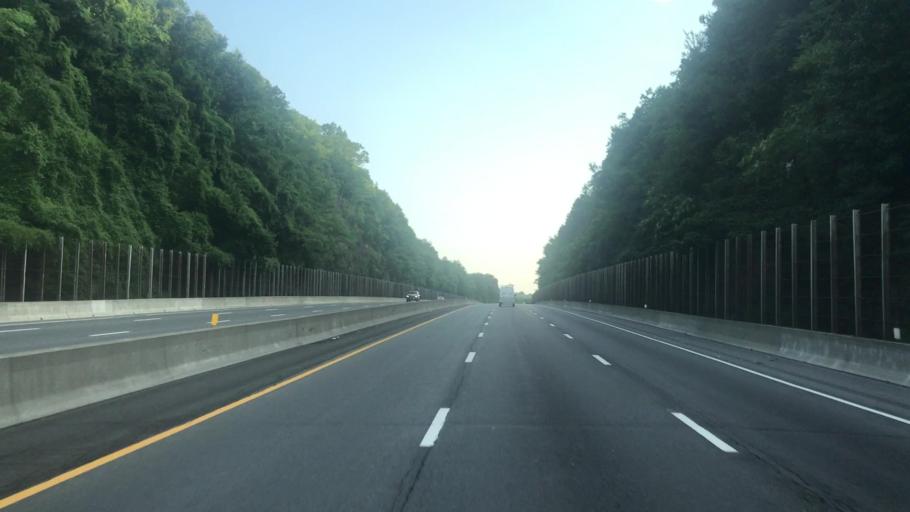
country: US
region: New York
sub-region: Westchester County
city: Ardsley
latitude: 40.9932
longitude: -73.8537
